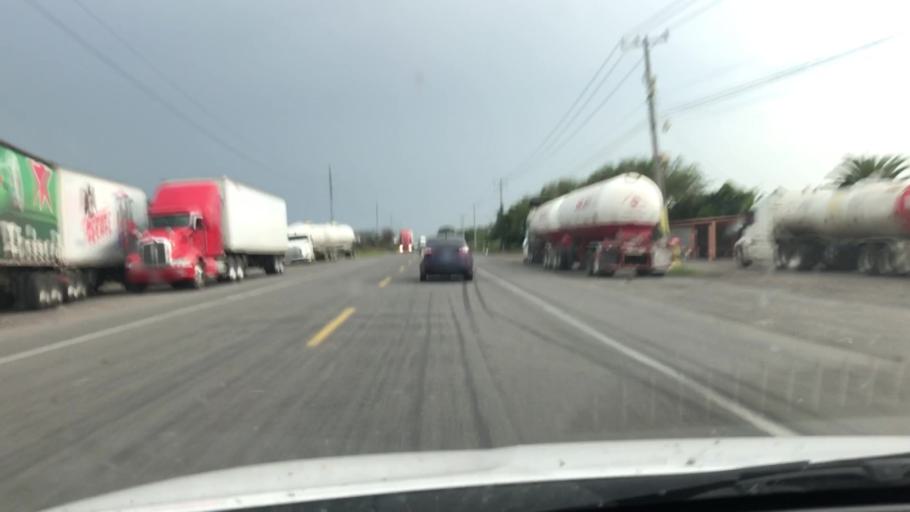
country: MX
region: Michoacan
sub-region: Vista Hermosa
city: Los Pilares
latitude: 20.2743
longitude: -102.4051
